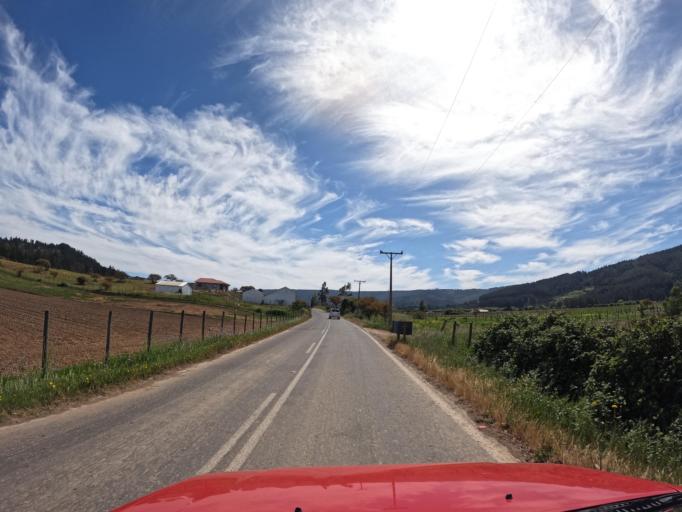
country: CL
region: Maule
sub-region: Provincia de Talca
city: Constitucion
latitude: -34.9906
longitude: -72.0003
